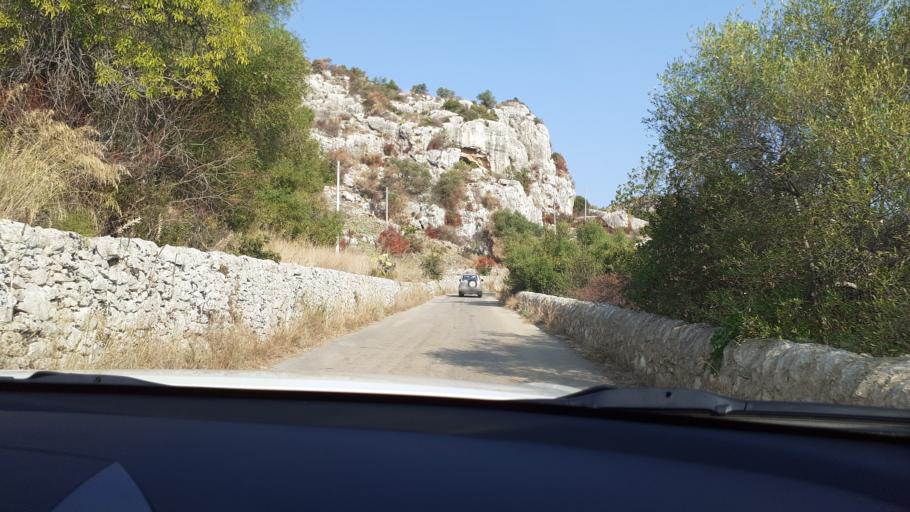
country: IT
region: Sicily
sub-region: Provincia di Siracusa
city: Cassibile
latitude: 36.9791
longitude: 15.1722
